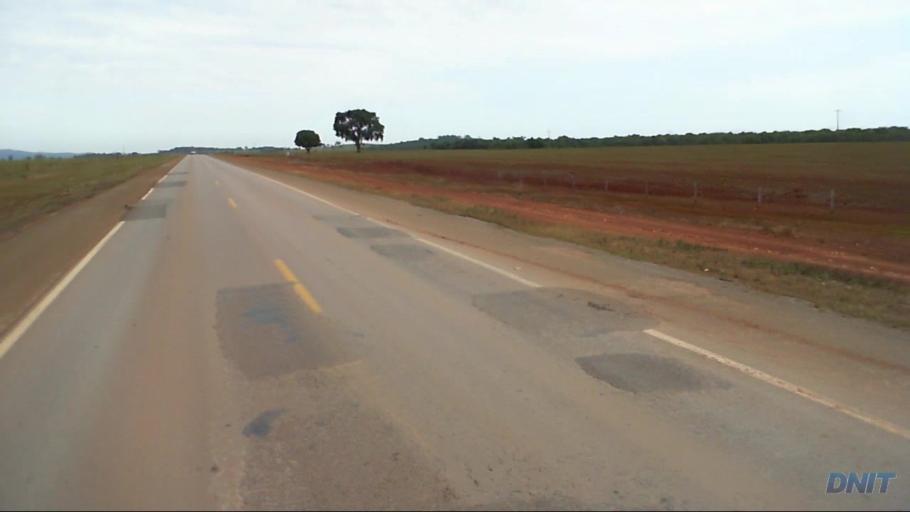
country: BR
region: Goias
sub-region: Uruacu
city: Uruacu
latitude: -14.6989
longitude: -49.1199
